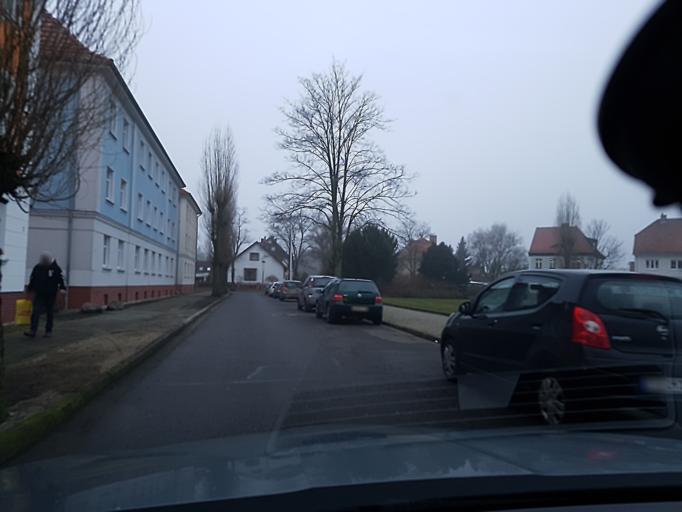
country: DE
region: Brandenburg
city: Finsterwalde
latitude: 51.6384
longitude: 13.7005
